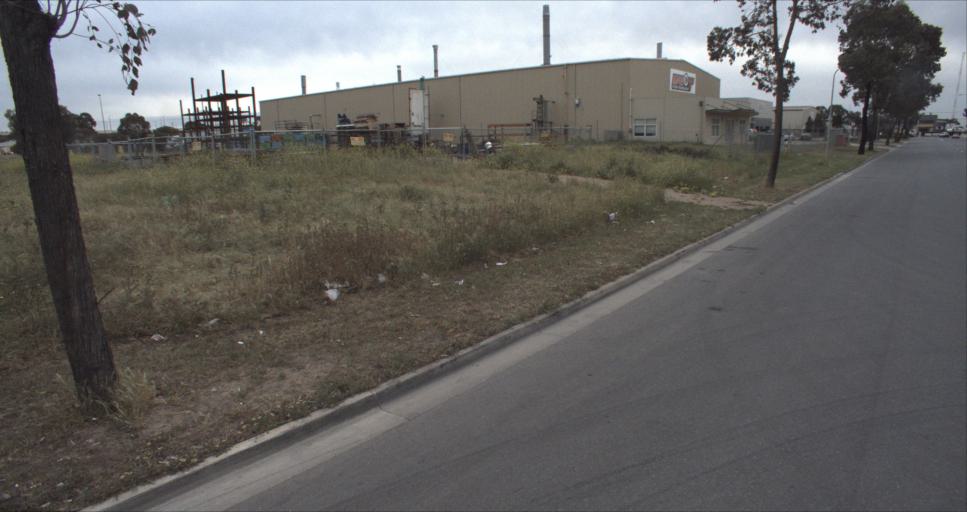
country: AU
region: South Australia
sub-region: Port Adelaide Enfield
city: Blair Athol
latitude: -34.8426
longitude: 138.5700
